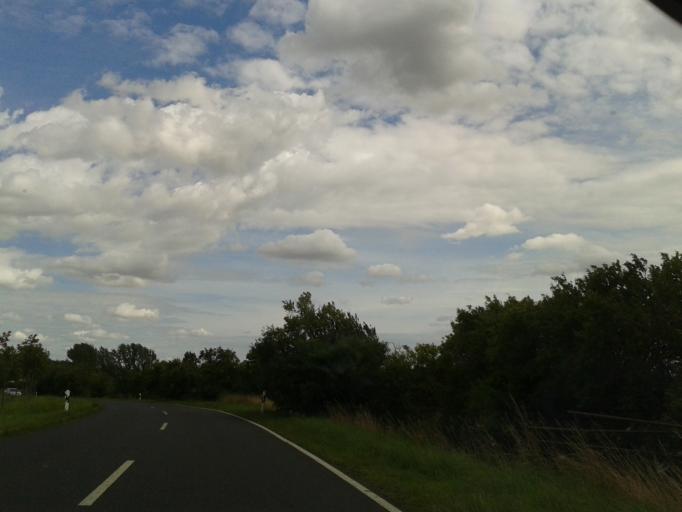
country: DE
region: Saxony-Anhalt
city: Peissen
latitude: 51.5103
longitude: 12.0283
